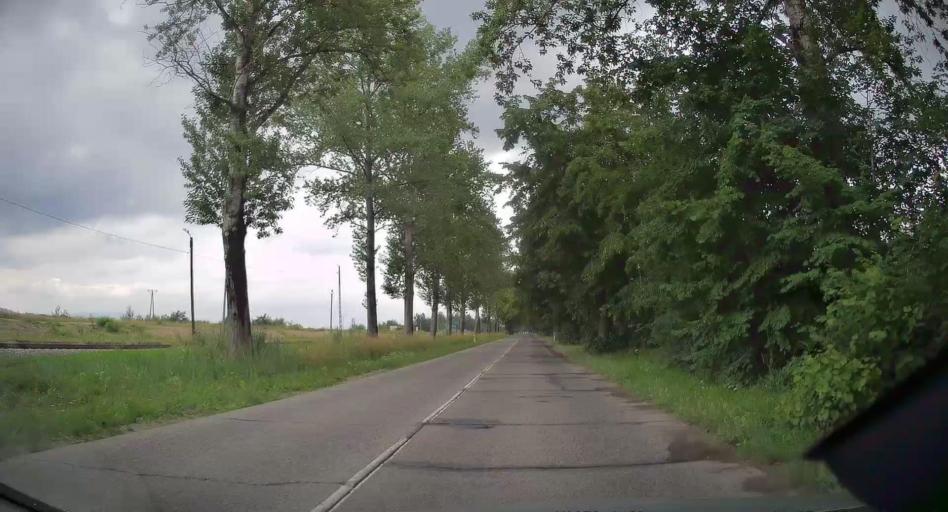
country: PL
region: Opole Voivodeship
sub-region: Powiat nyski
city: Paczkow
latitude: 50.4800
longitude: 16.9975
